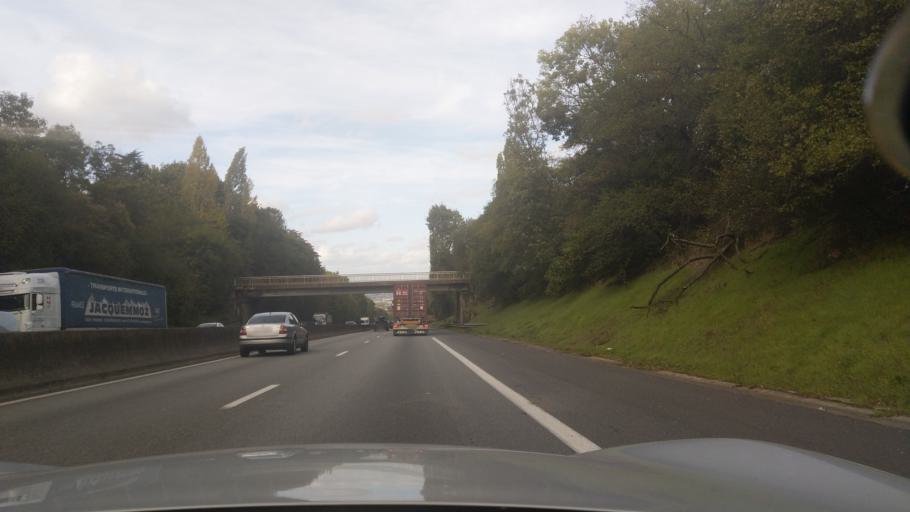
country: FR
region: Ile-de-France
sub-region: Departement des Yvelines
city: Orgeval
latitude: 48.9097
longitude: 2.0054
